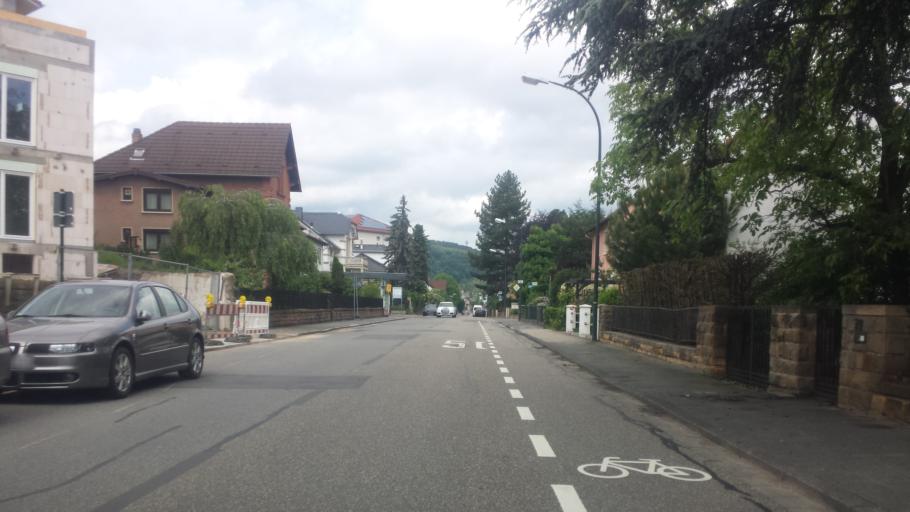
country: DE
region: Rheinland-Pfalz
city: Bad Duerkheim
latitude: 49.4545
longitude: 8.1755
